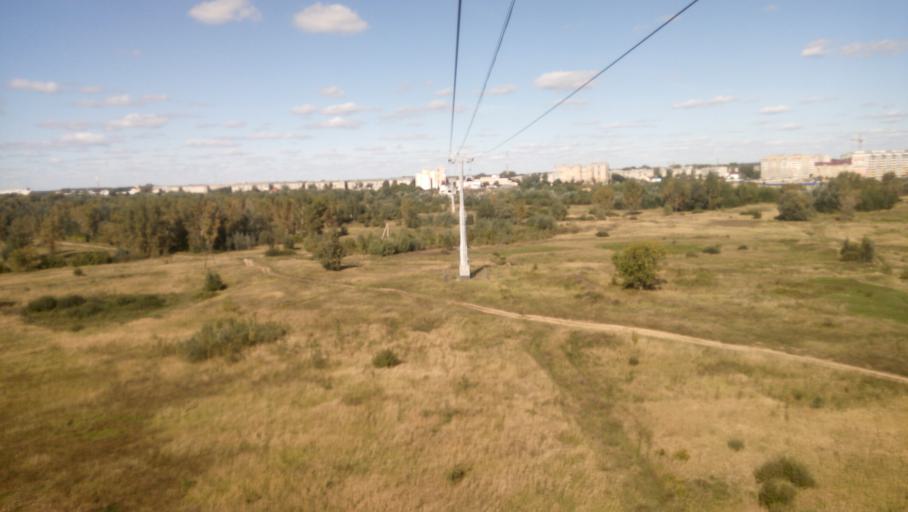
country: RU
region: Nizjnij Novgorod
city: Bor
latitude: 56.3453
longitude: 44.0548
